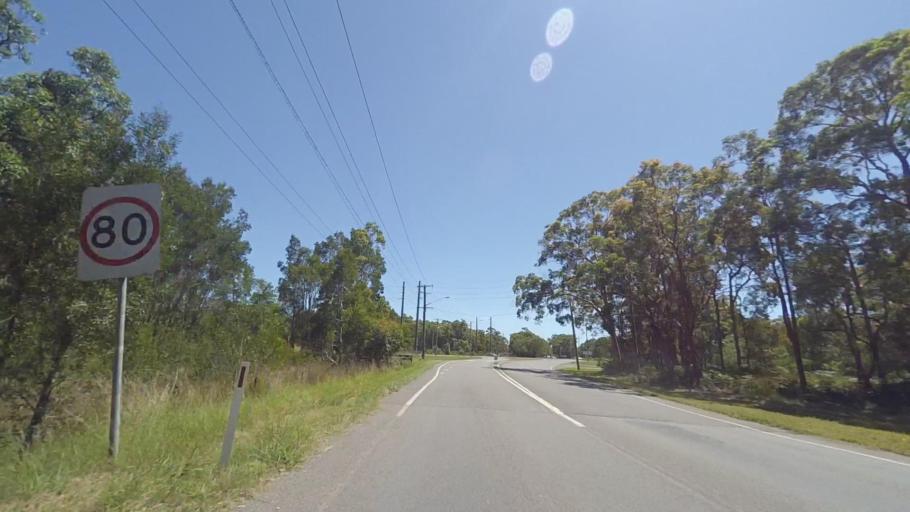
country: AU
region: New South Wales
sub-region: Port Stephens Shire
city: Medowie
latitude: -32.7735
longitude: 151.8593
